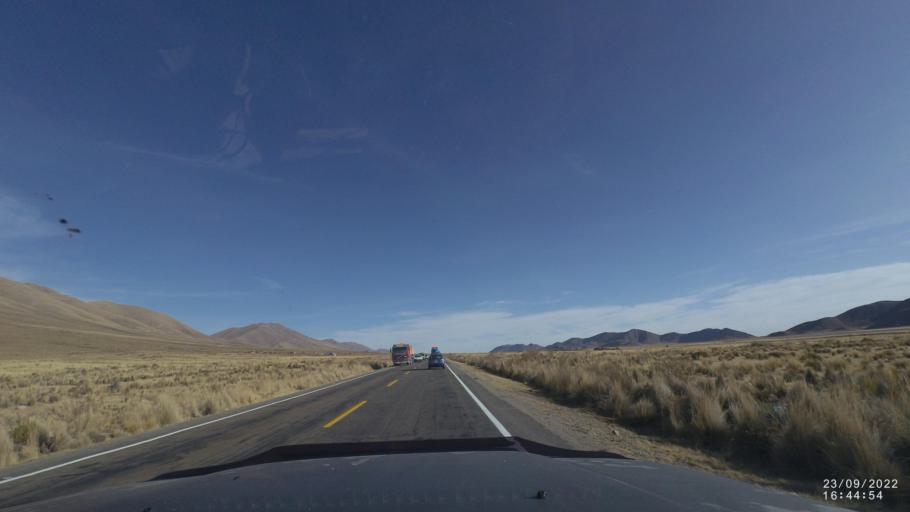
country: BO
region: Oruro
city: Poopo
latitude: -18.3348
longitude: -66.9869
